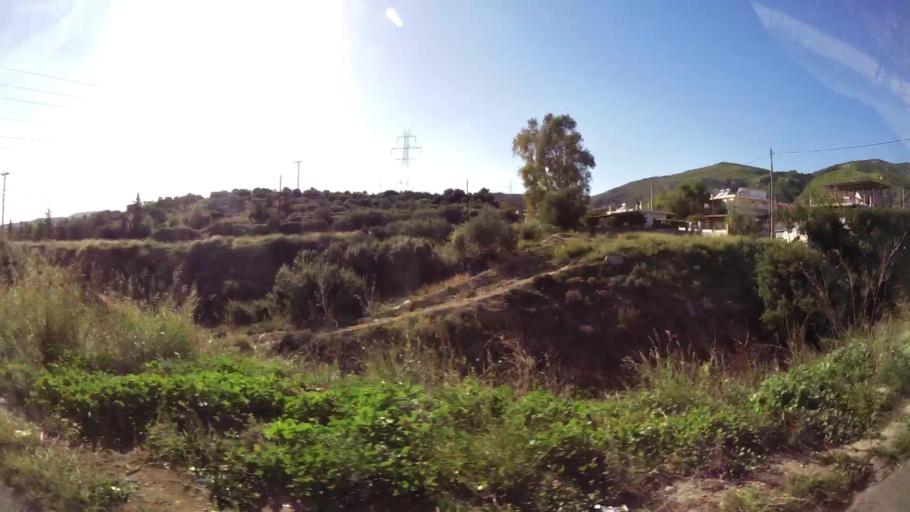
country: GR
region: Attica
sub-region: Nomarchia Anatolikis Attikis
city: Acharnes
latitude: 38.1014
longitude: 23.7239
